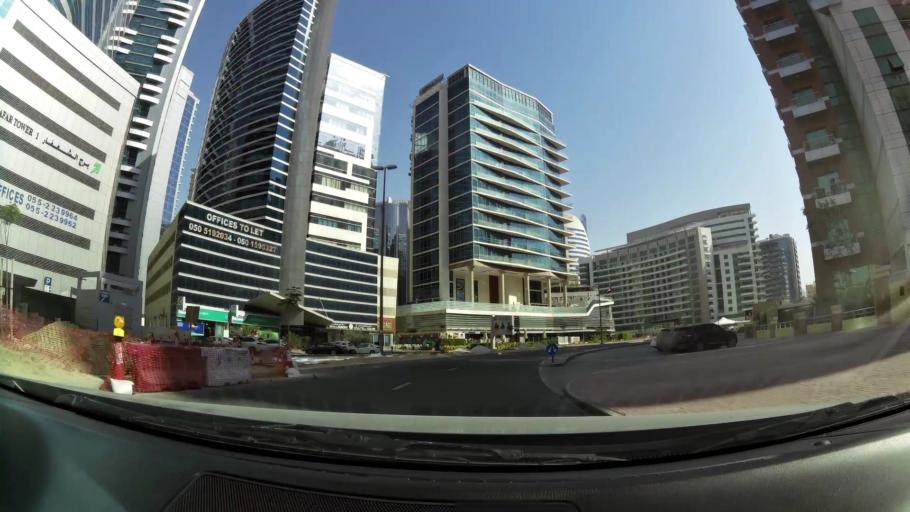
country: AE
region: Dubai
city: Dubai
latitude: 25.0986
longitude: 55.1736
